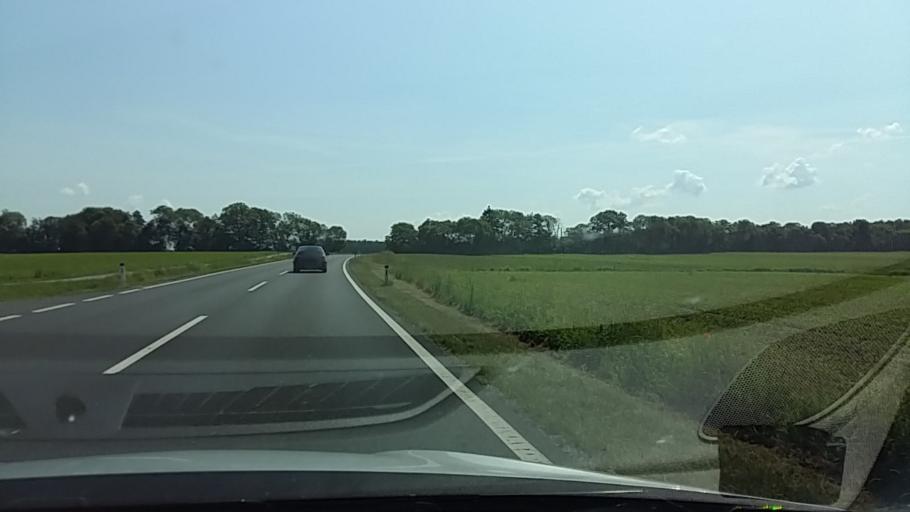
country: AT
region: Burgenland
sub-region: Politischer Bezirk Jennersdorf
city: Weichselbaum
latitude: 46.9460
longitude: 16.2039
